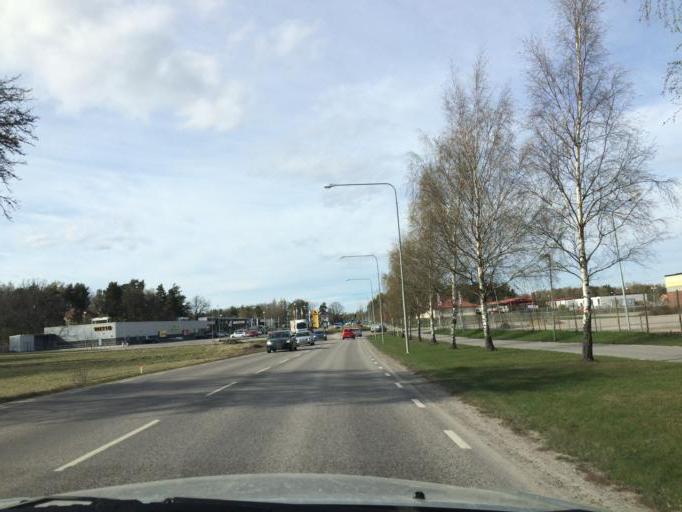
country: SE
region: Soedermanland
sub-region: Eskilstuna Kommun
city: Torshalla
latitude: 59.4091
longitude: 16.4777
